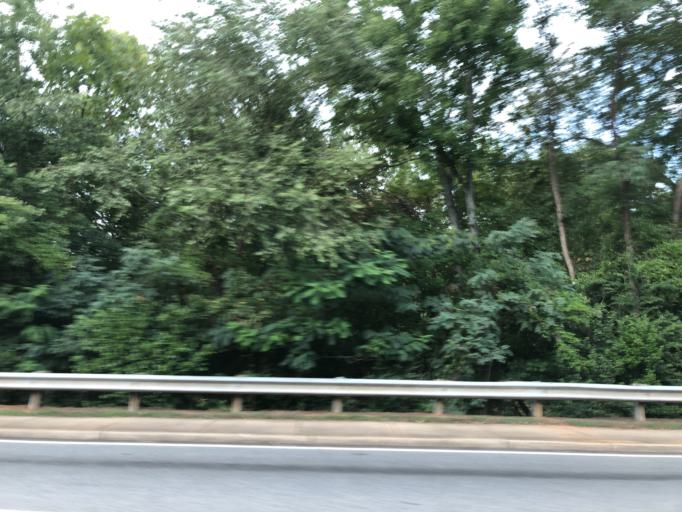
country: US
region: Georgia
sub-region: Clarke County
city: Athens
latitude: 33.9541
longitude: -83.3674
